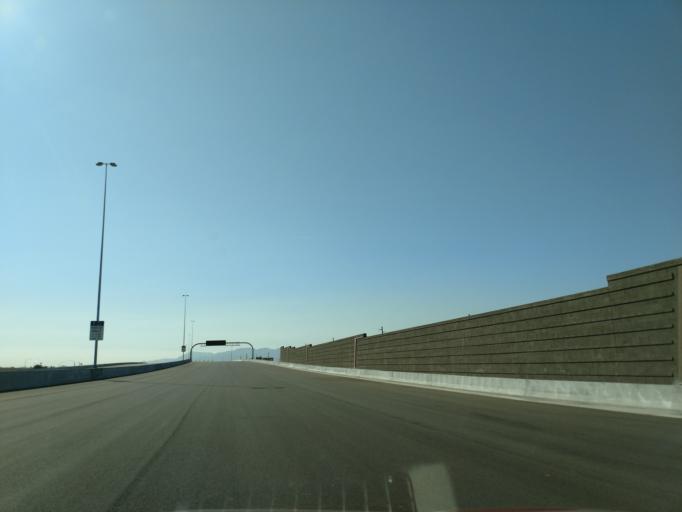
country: US
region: Arizona
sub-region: Maricopa County
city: Tolleson
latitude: 33.4549
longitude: -112.1849
